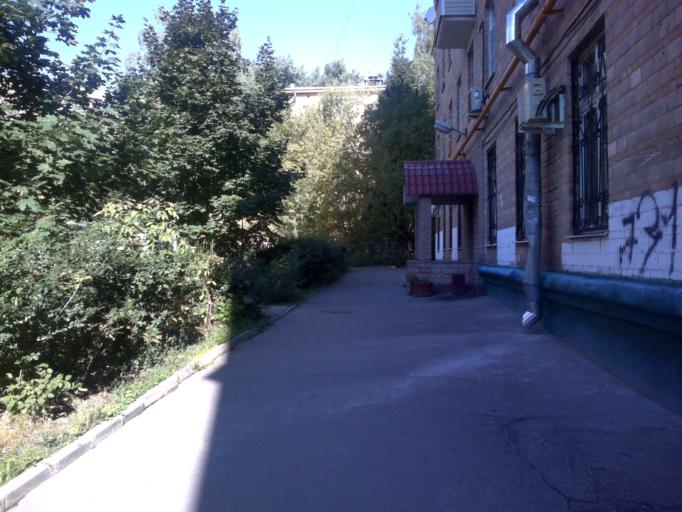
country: RU
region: Moskovskaya
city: Leninskiye Gory
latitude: 55.6937
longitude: 37.5712
